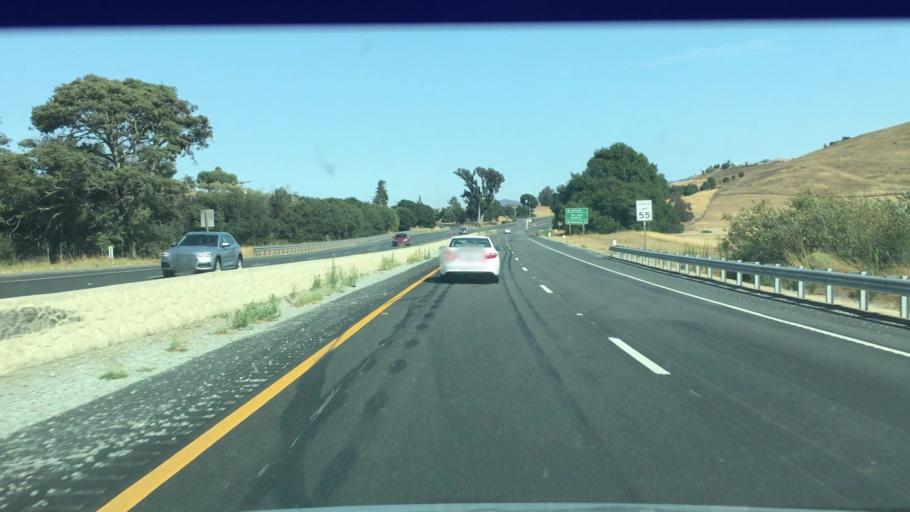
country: US
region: California
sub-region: San Benito County
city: San Juan Bautista
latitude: 36.8469
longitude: -121.5501
